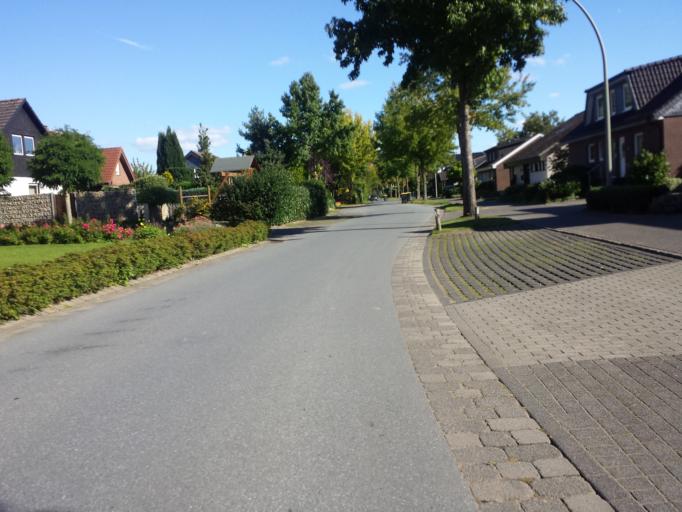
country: DE
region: North Rhine-Westphalia
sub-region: Regierungsbezirk Detmold
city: Langenberg
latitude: 51.7645
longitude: 8.3145
